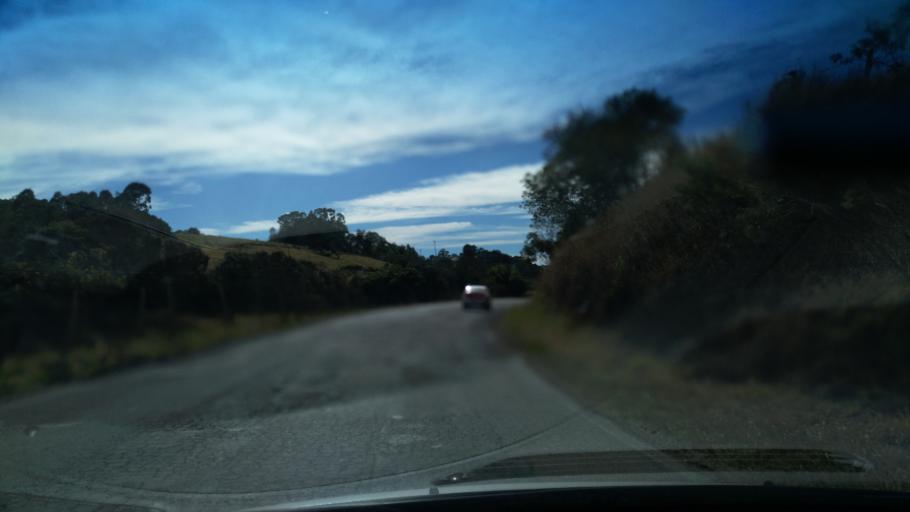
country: BR
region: Minas Gerais
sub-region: Andradas
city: Andradas
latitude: -22.0396
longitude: -46.3508
